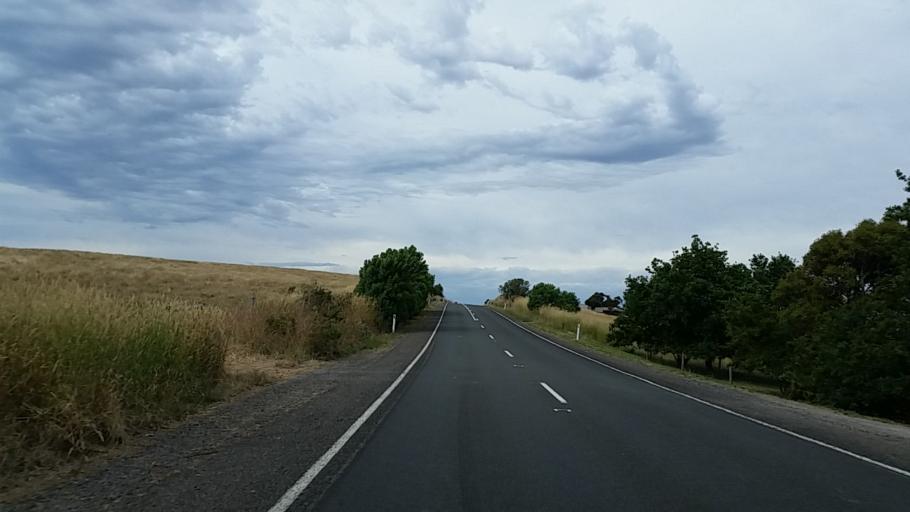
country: AU
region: South Australia
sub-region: Onkaparinga
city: Port Willunga
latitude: -35.3841
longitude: 138.4350
